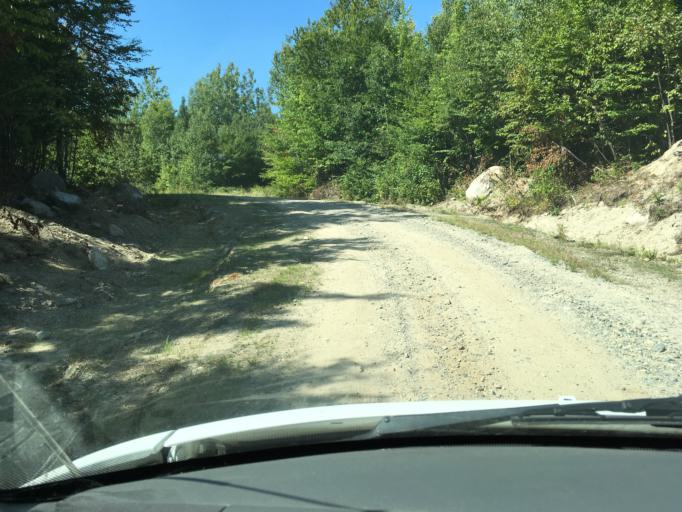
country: US
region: Maine
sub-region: Penobscot County
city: Millinocket
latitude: 45.8464
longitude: -68.7262
